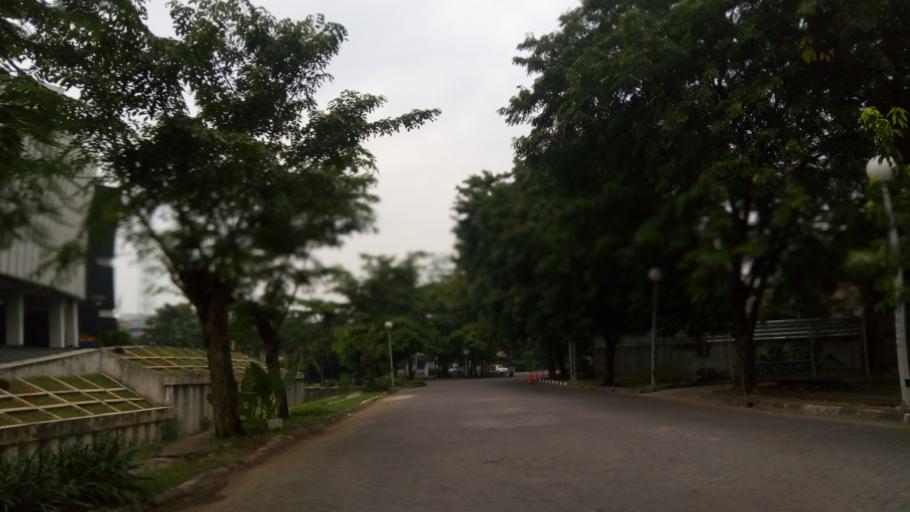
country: ID
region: Jakarta Raya
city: Jakarta
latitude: -6.1514
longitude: 106.8412
